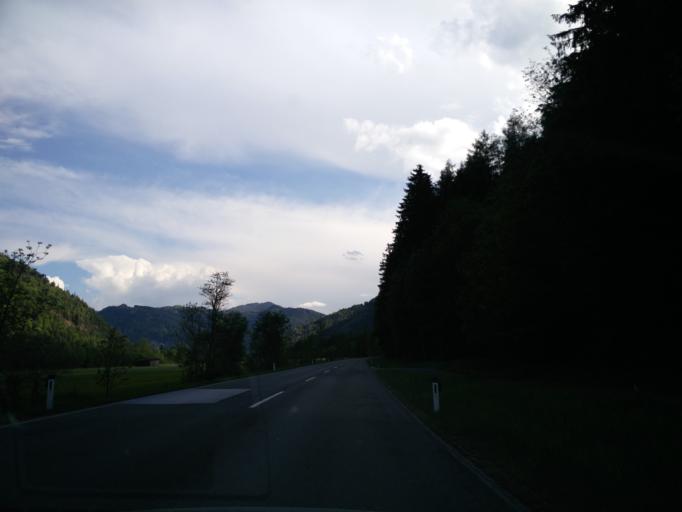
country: AT
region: Tyrol
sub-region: Politischer Bezirk Kitzbuhel
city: Kirchdorf in Tirol
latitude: 47.6083
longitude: 12.4679
